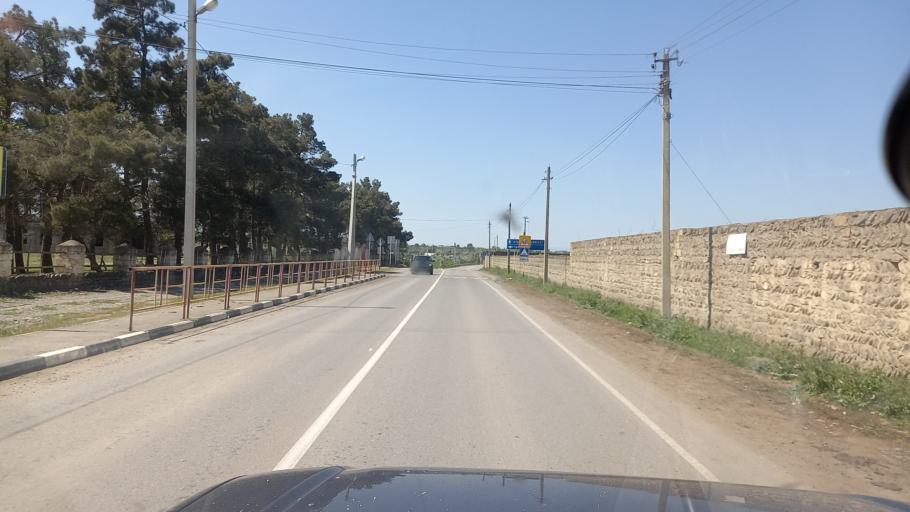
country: AZ
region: Qusar
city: Samur
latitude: 41.7261
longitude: 48.4572
